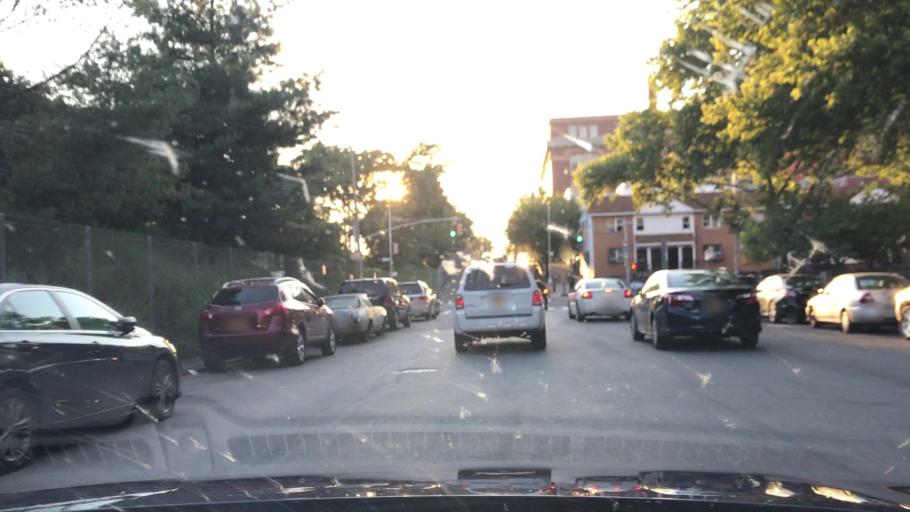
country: US
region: New York
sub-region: New York County
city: Manhattan
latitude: 40.8054
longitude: -73.9200
